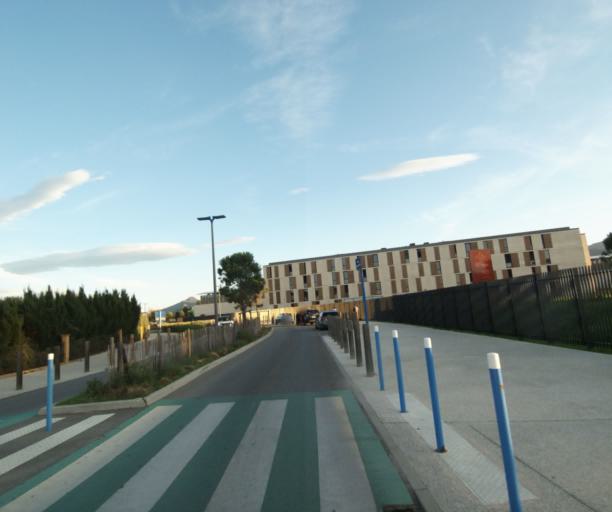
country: FR
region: Languedoc-Roussillon
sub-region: Departement des Pyrenees-Orientales
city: Argelers
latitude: 42.5671
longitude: 3.0056
